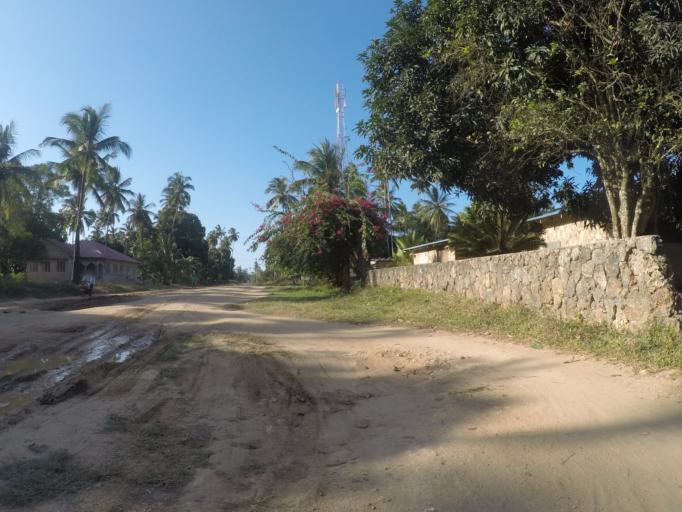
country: TZ
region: Zanzibar Central/South
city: Koani
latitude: -6.1599
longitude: 39.2874
